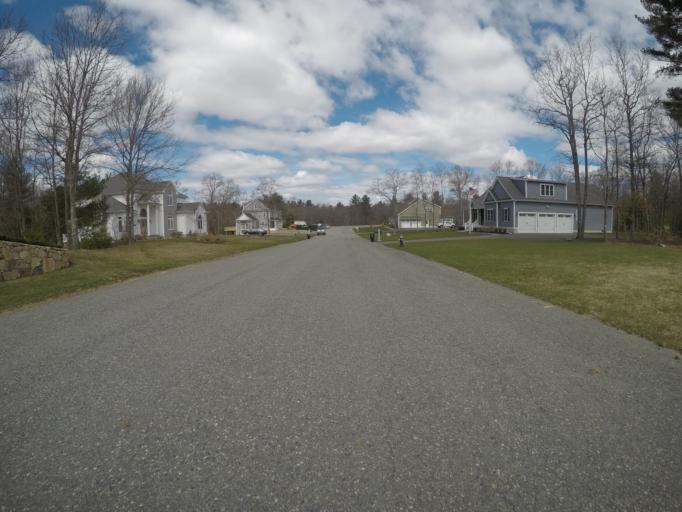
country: US
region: Massachusetts
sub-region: Norfolk County
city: Stoughton
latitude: 42.0801
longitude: -71.0761
